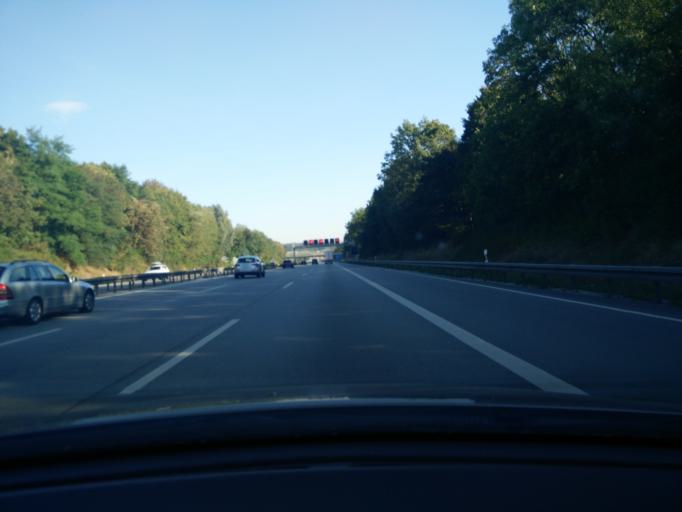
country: DE
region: Bavaria
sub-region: Upper Bavaria
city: Allershausen
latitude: 48.4309
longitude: 11.5895
